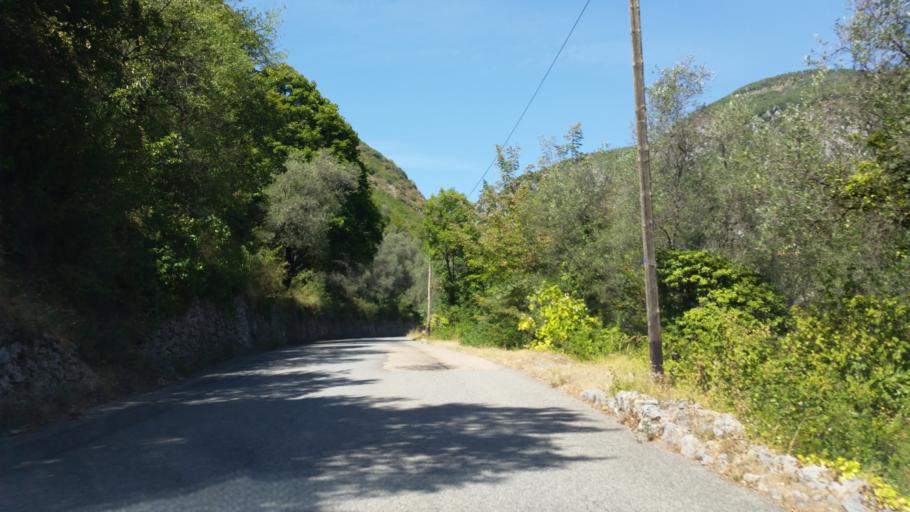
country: FR
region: Provence-Alpes-Cote d'Azur
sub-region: Departement des Alpes-Maritimes
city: Breil-sur-Roya
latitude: 43.9531
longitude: 7.5165
